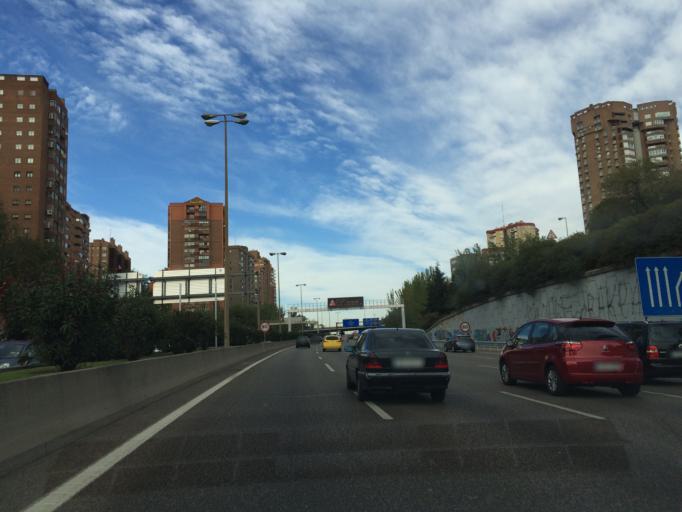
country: ES
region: Madrid
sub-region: Provincia de Madrid
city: Pinar de Chamartin
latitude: 40.4773
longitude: -3.6744
